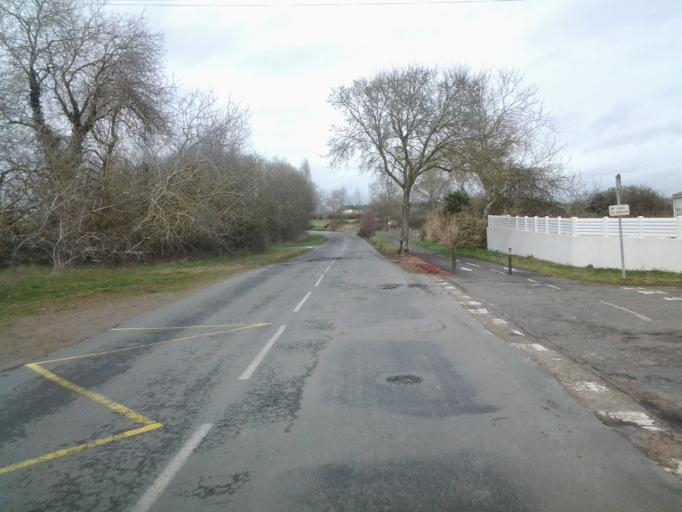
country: FR
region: Pays de la Loire
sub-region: Departement de la Vendee
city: La Tranche-sur-Mer
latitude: 46.3563
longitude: -1.4538
